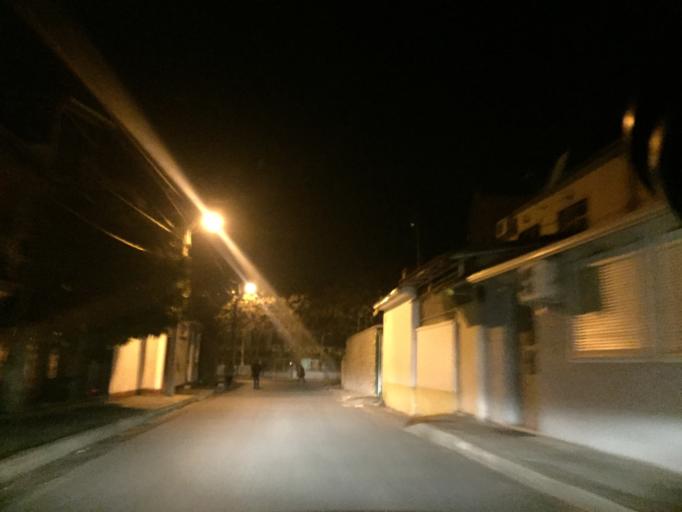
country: AL
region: Shkoder
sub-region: Rrethi i Shkodres
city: Shkoder
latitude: 42.0696
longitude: 19.5027
